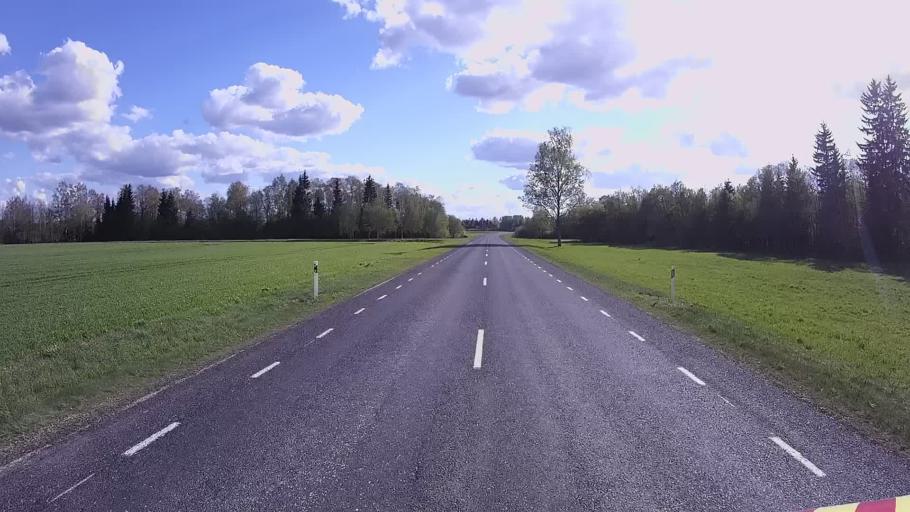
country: EE
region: Jogevamaa
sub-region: Poltsamaa linn
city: Poltsamaa
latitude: 58.7143
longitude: 26.1788
